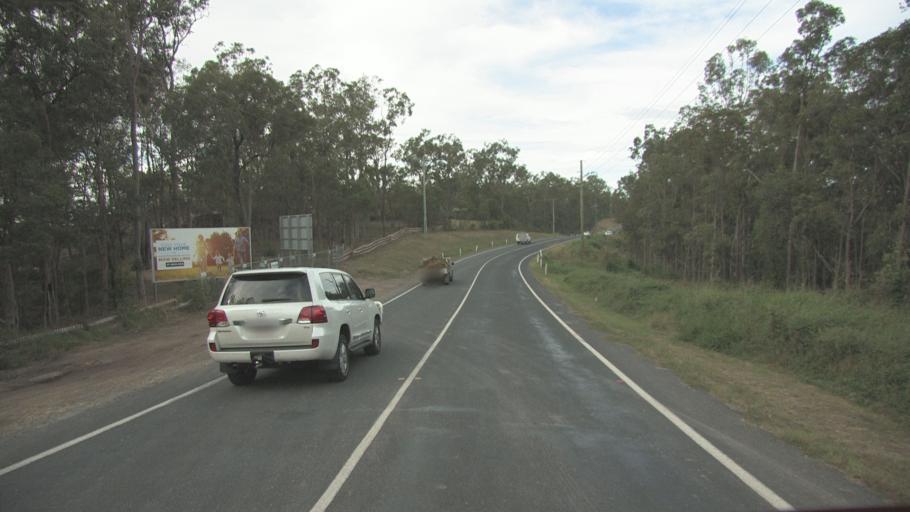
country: AU
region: Queensland
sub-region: Logan
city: Windaroo
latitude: -27.7259
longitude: 153.1687
